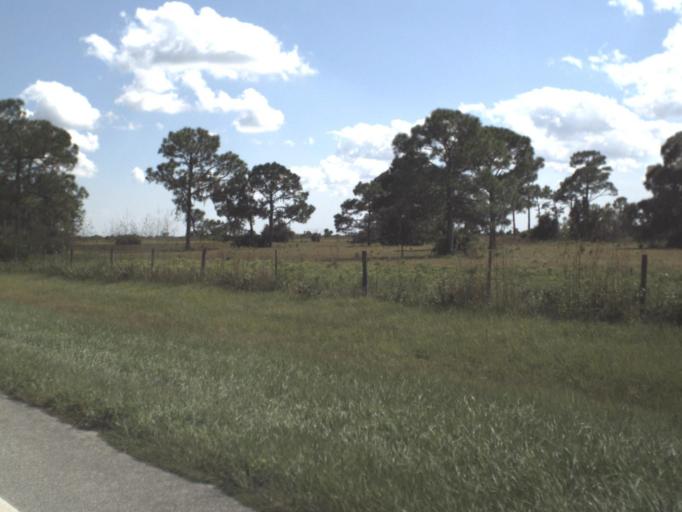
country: US
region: Florida
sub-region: Highlands County
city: Lake Placid
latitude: 27.3736
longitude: -81.0879
